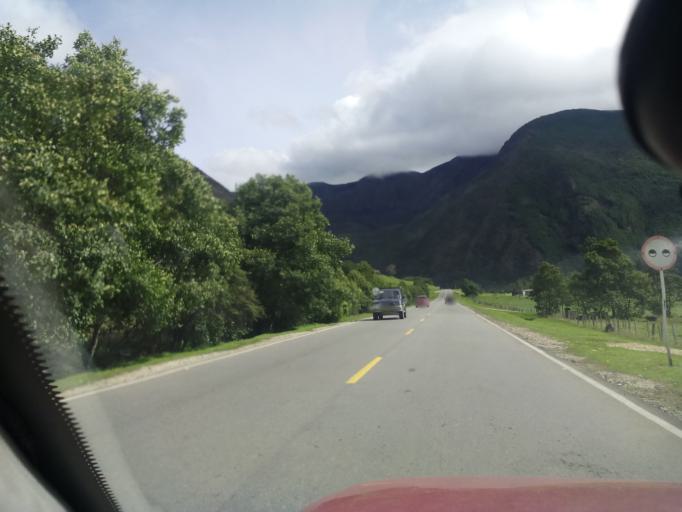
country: CO
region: Boyaca
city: Arcabuco
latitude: 5.7120
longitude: -73.3737
